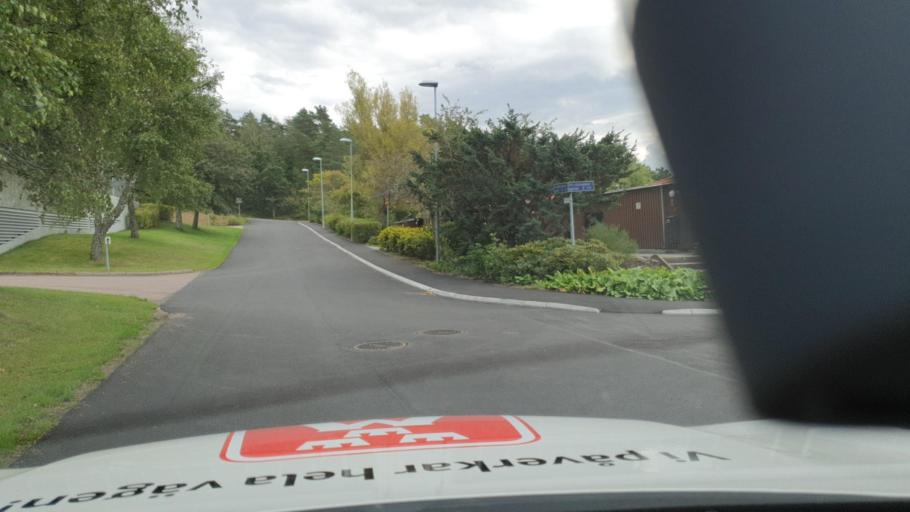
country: SE
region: Vaestra Goetaland
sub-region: Goteborg
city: Loevgaerdet
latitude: 57.8133
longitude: 12.0499
